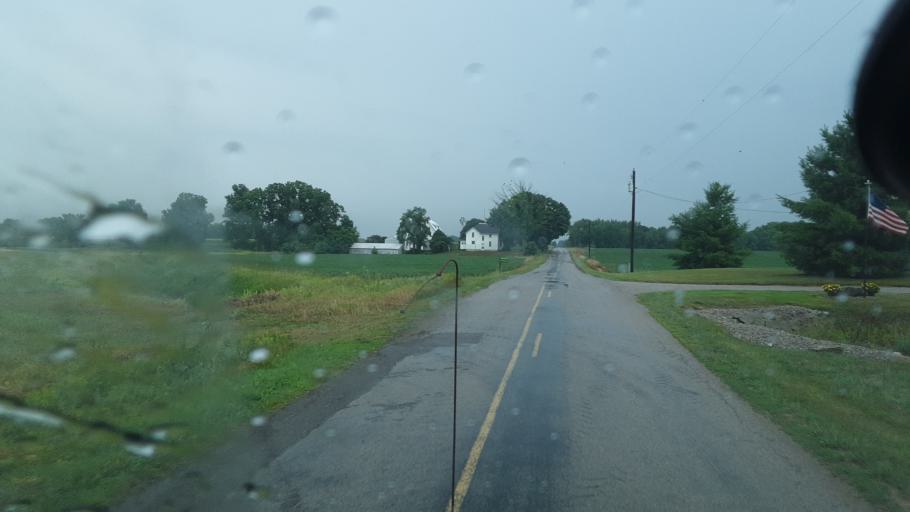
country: US
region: Ohio
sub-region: Williams County
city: Edgerton
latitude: 41.4912
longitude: -84.8147
